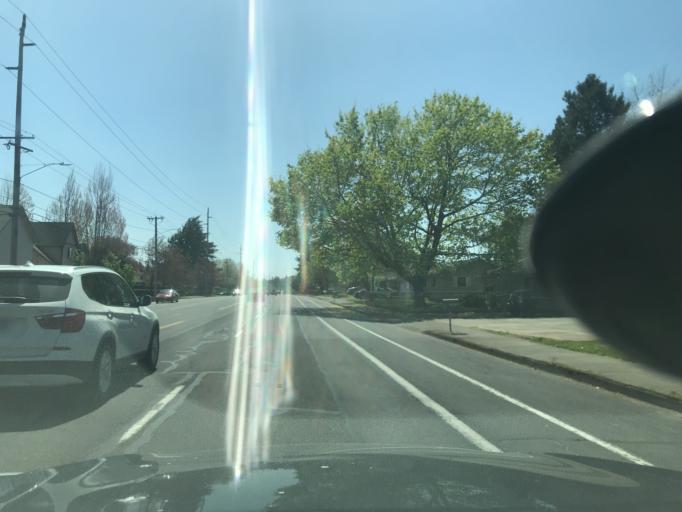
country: US
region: Oregon
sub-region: Multnomah County
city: Gresham
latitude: 45.5110
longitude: -122.4758
